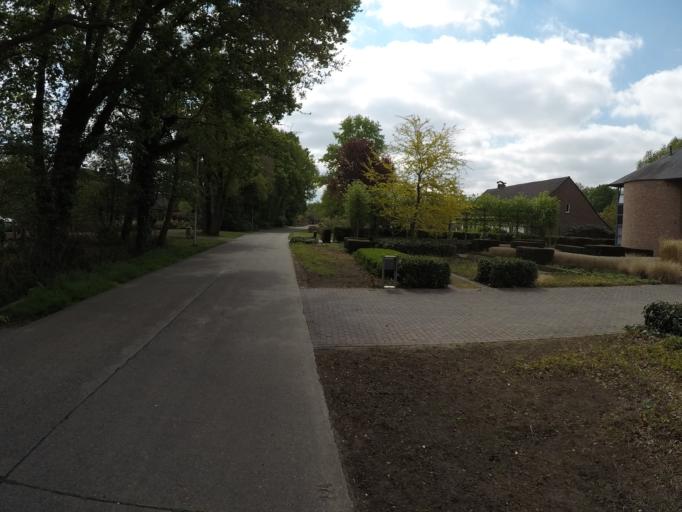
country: BE
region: Flanders
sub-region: Provincie Antwerpen
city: Nijlen
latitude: 51.1538
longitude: 4.6336
